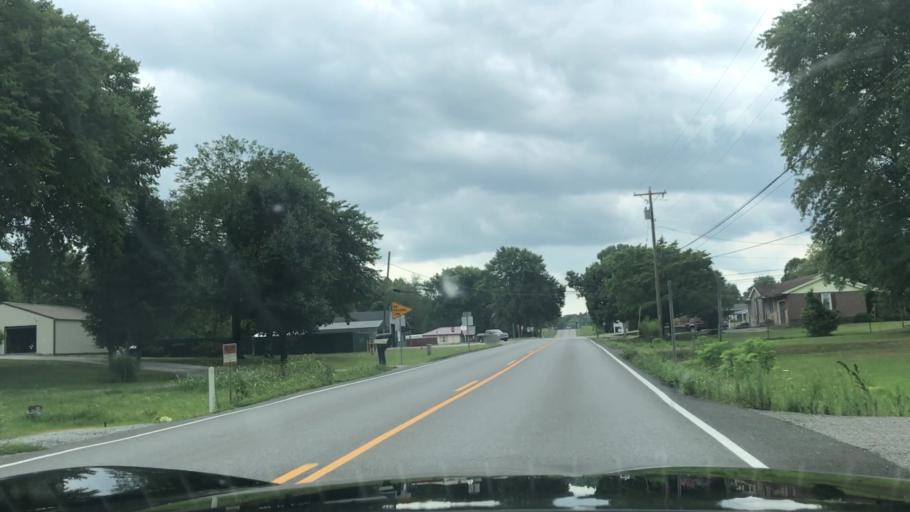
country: US
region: Kentucky
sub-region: Muhlenberg County
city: Central City
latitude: 37.1985
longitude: -87.0368
